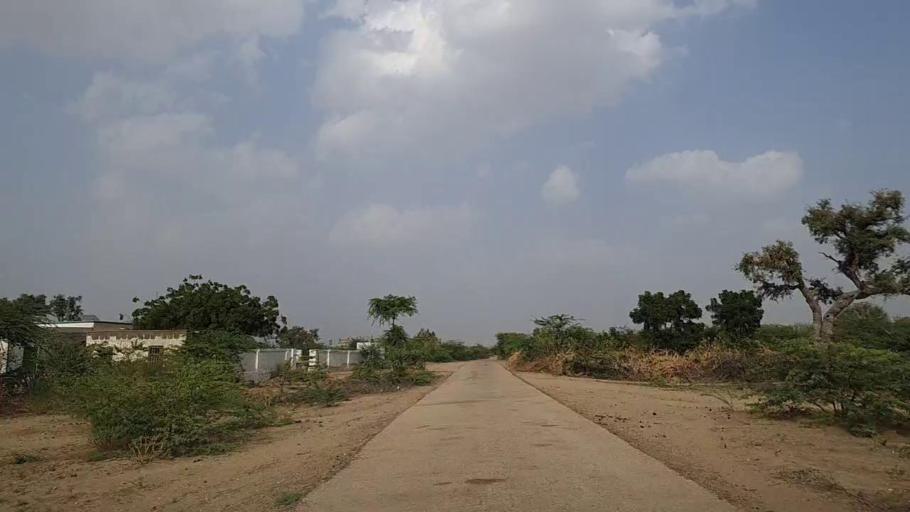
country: PK
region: Sindh
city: Islamkot
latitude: 24.8662
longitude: 70.1115
